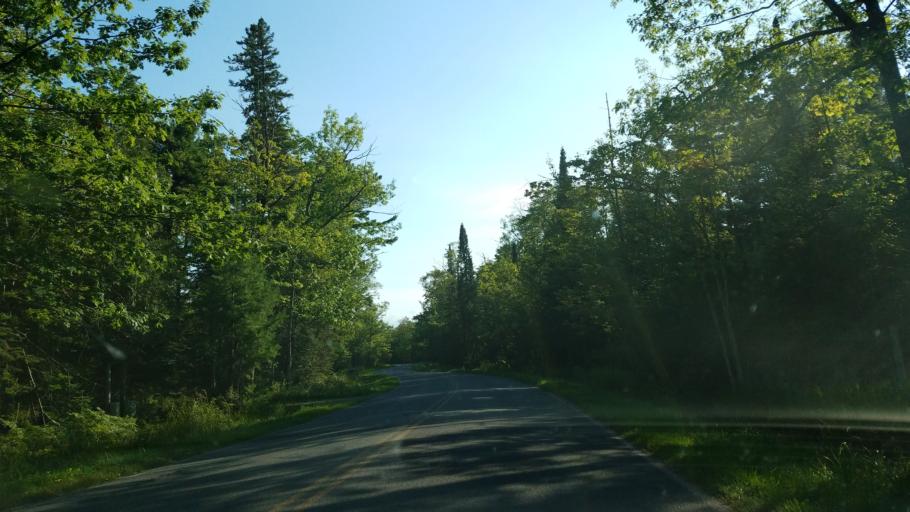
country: US
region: Wisconsin
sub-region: Bayfield County
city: Washburn
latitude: 46.7626
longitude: -90.7549
